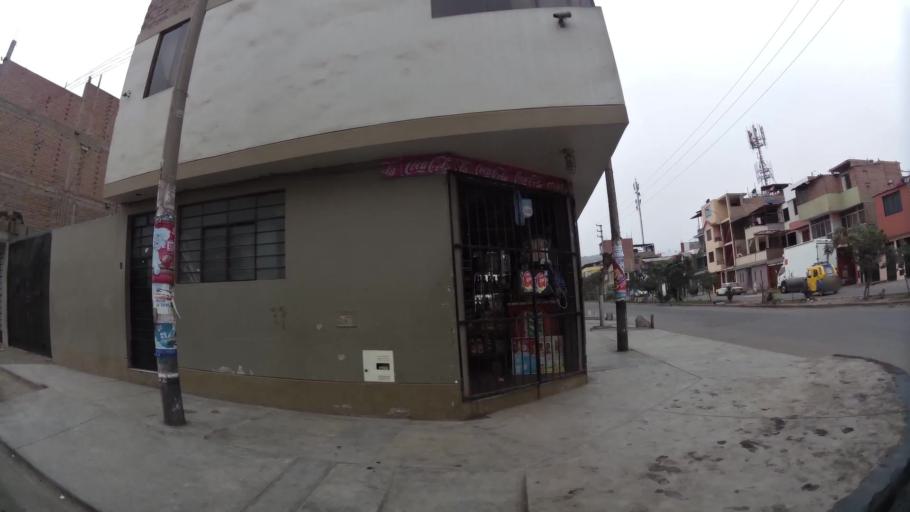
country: PE
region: Lima
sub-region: Lima
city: Surco
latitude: -12.1728
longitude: -76.9689
